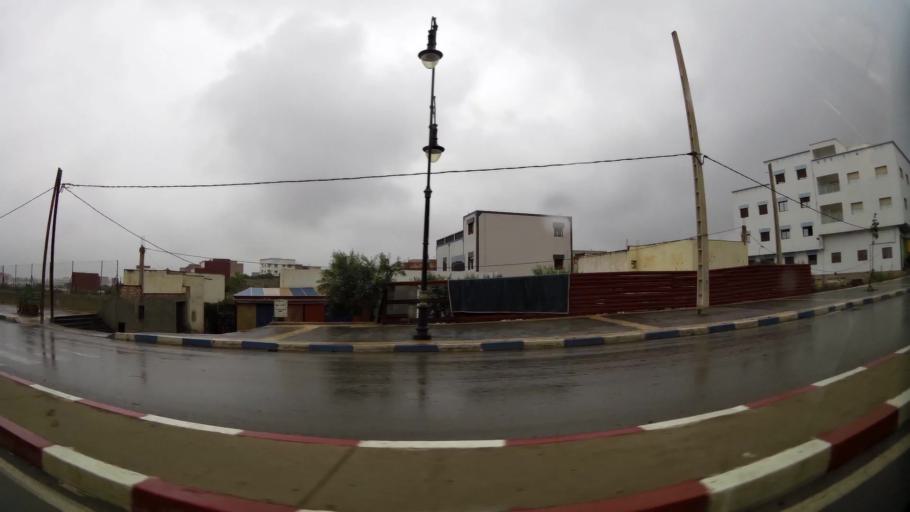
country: MA
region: Taza-Al Hoceima-Taounate
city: Imzourene
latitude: 35.1451
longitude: -3.8481
